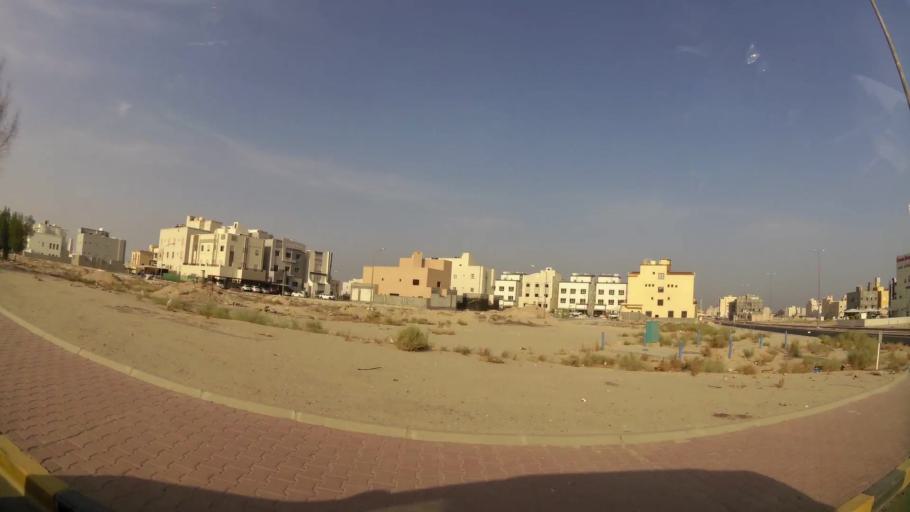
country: KW
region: Mubarak al Kabir
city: Mubarak al Kabir
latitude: 29.1933
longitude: 48.0975
